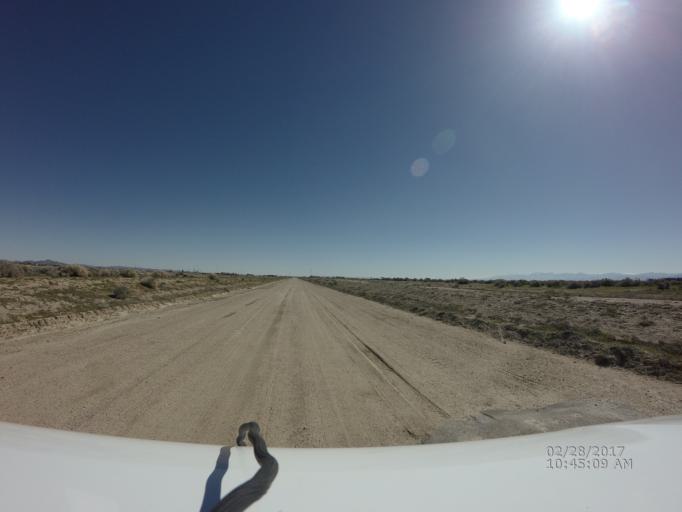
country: US
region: California
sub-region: Kern County
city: Rosamond
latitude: 34.8055
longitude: -118.2789
